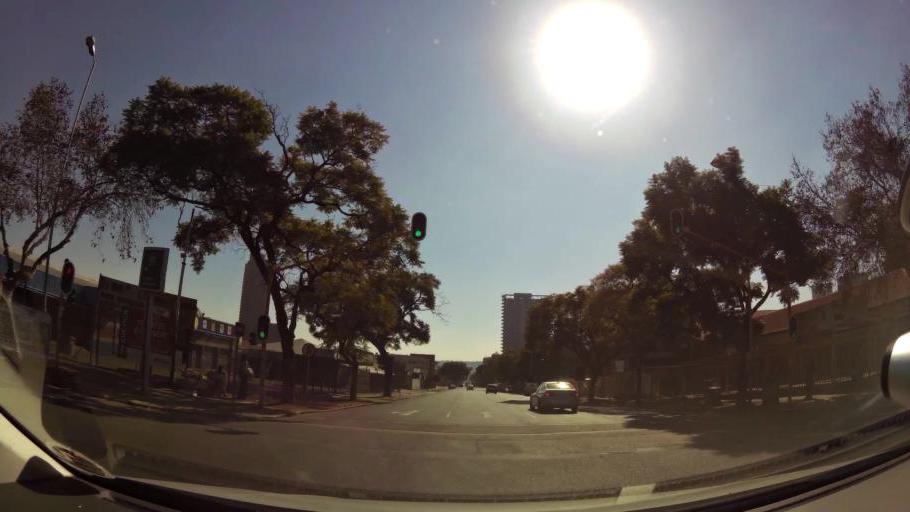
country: ZA
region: Gauteng
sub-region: City of Tshwane Metropolitan Municipality
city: Pretoria
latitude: -25.7483
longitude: 28.1808
